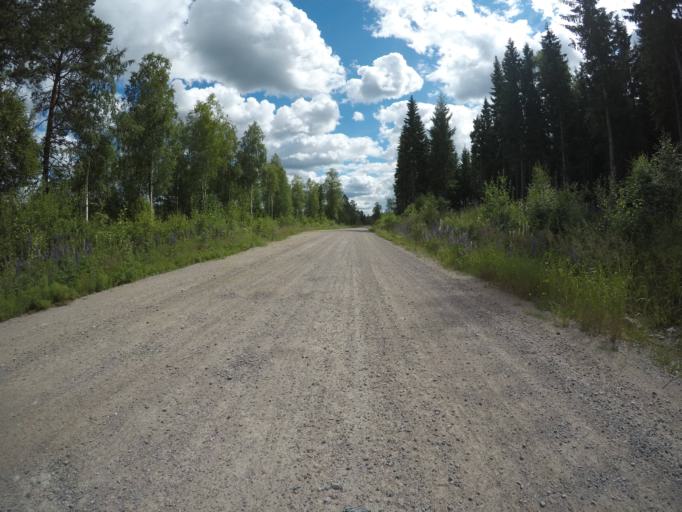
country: SE
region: Vaermland
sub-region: Filipstads Kommun
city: Lesjofors
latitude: 60.1283
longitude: 14.4251
